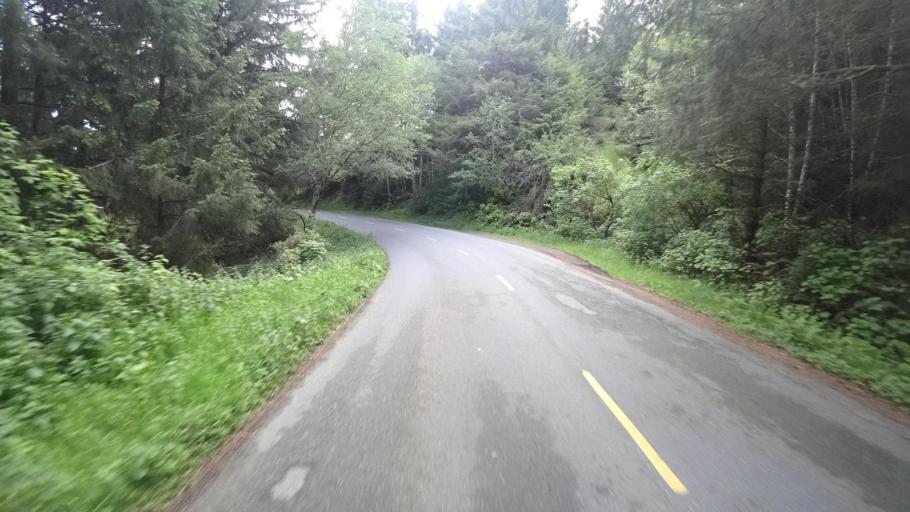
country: US
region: California
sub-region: Humboldt County
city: Ferndale
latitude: 40.5472
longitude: -124.2757
